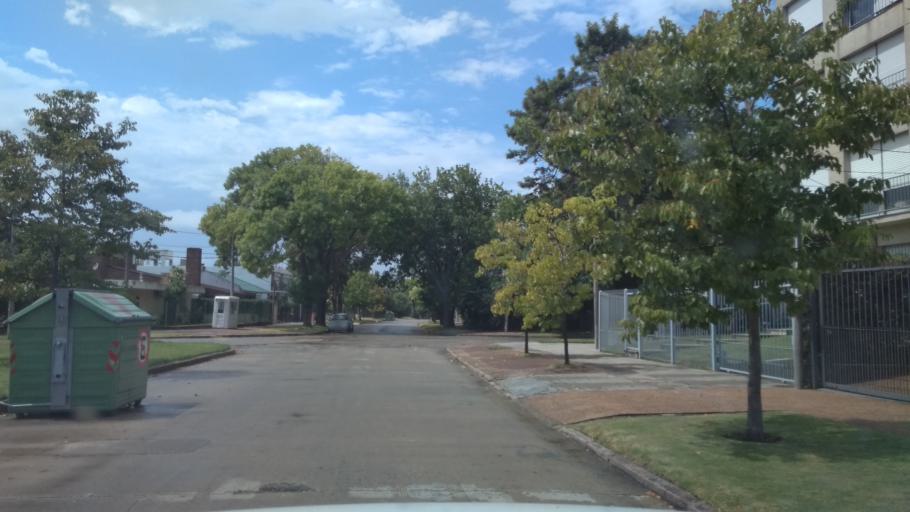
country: UY
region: Canelones
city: Paso de Carrasco
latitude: -34.8939
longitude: -56.0762
